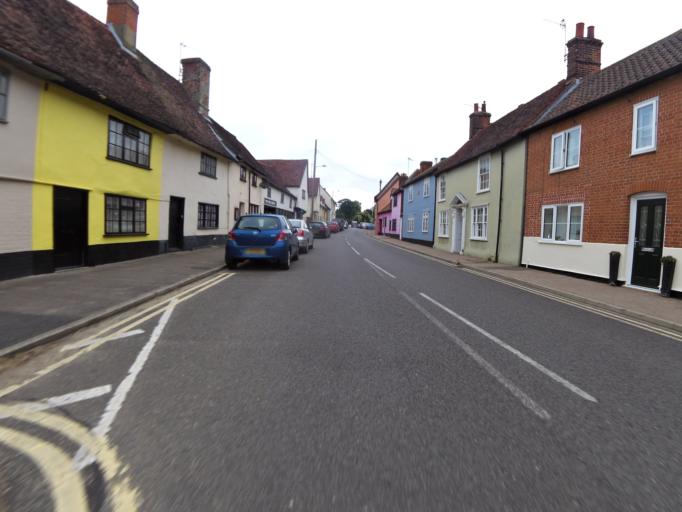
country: GB
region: England
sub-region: Suffolk
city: Bramford
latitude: 52.0763
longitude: 1.0969
